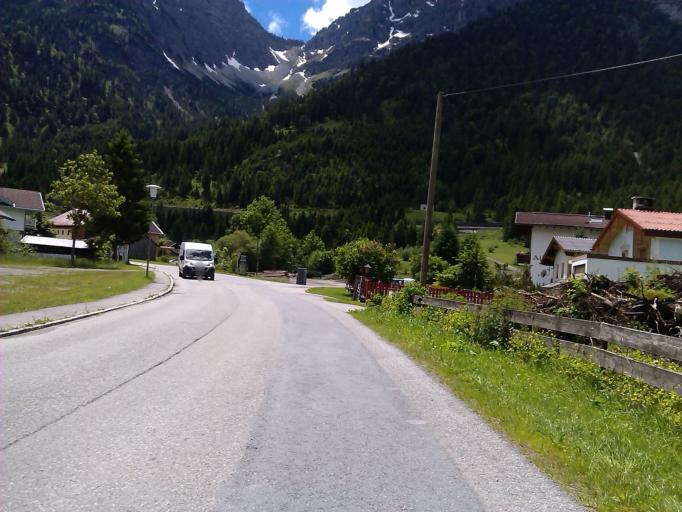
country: AT
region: Tyrol
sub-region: Politischer Bezirk Reutte
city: Heiterwang
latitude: 47.4467
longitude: 10.7433
